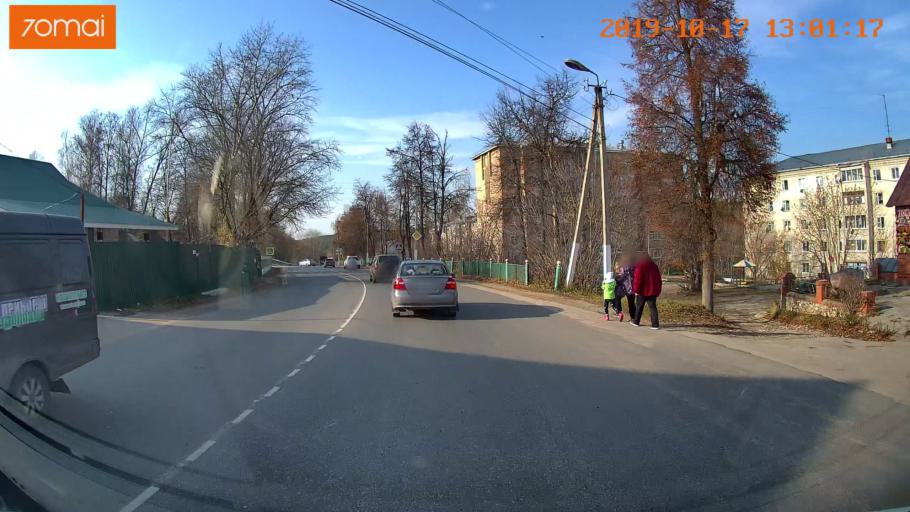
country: RU
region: Rjazan
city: Kasimov
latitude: 54.9455
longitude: 41.3719
